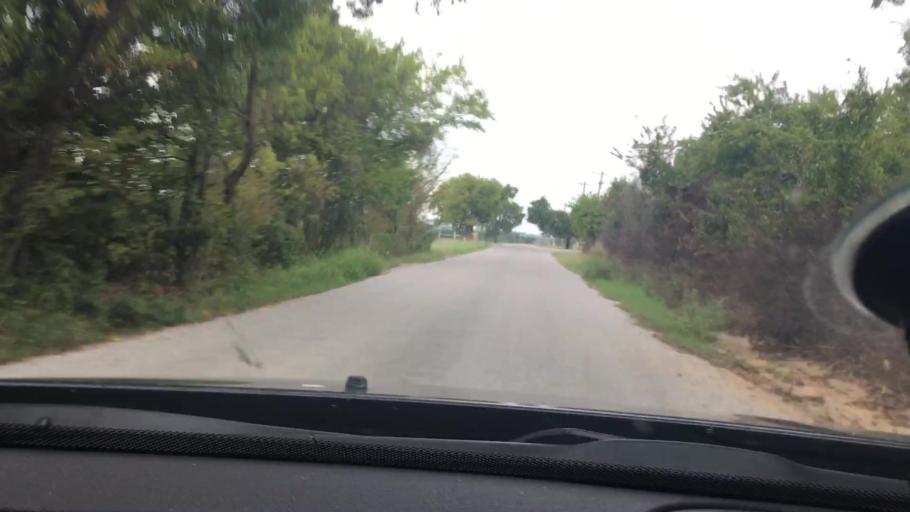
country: US
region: Oklahoma
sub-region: Carter County
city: Lone Grove
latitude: 34.1281
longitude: -97.2128
